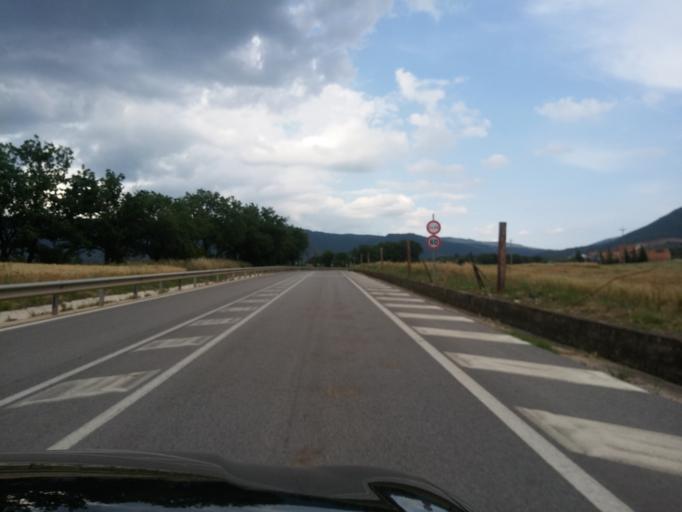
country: IT
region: Apulia
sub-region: Provincia di Foggia
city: Rignano Garganico
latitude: 41.7149
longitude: 15.5359
